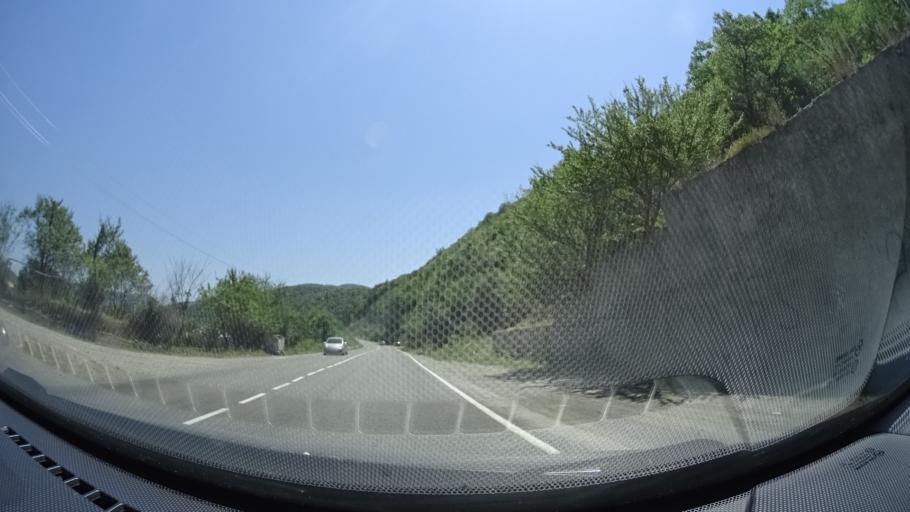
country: GE
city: Zhinvali
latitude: 42.1671
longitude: 44.6978
